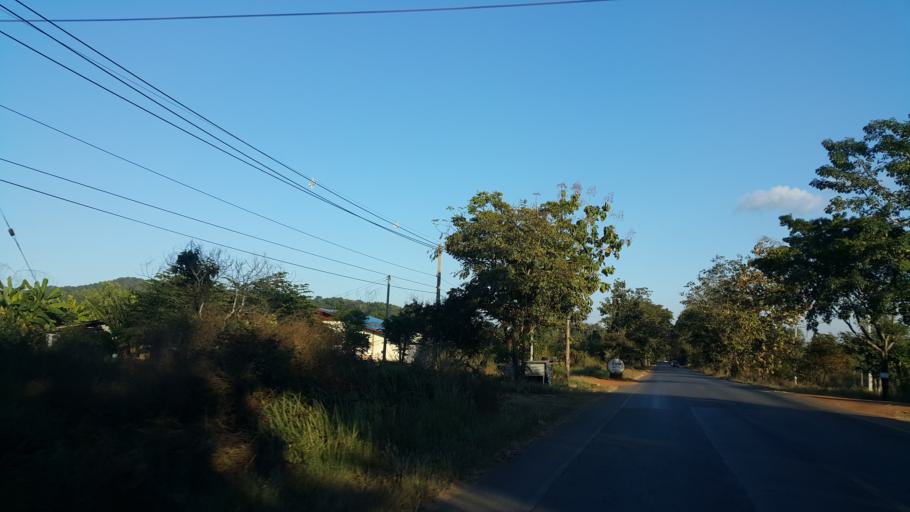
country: TH
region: Sukhothai
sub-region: Amphoe Si Satchanalai
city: Si Satchanalai
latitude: 17.5505
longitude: 99.8869
